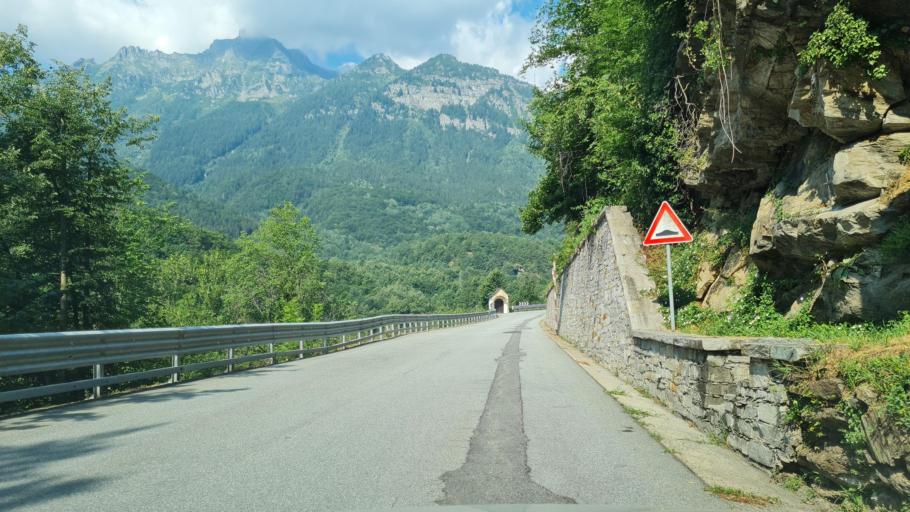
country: IT
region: Piedmont
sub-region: Provincia Verbano-Cusio-Ossola
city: Baceno
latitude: 46.2682
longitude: 8.3124
